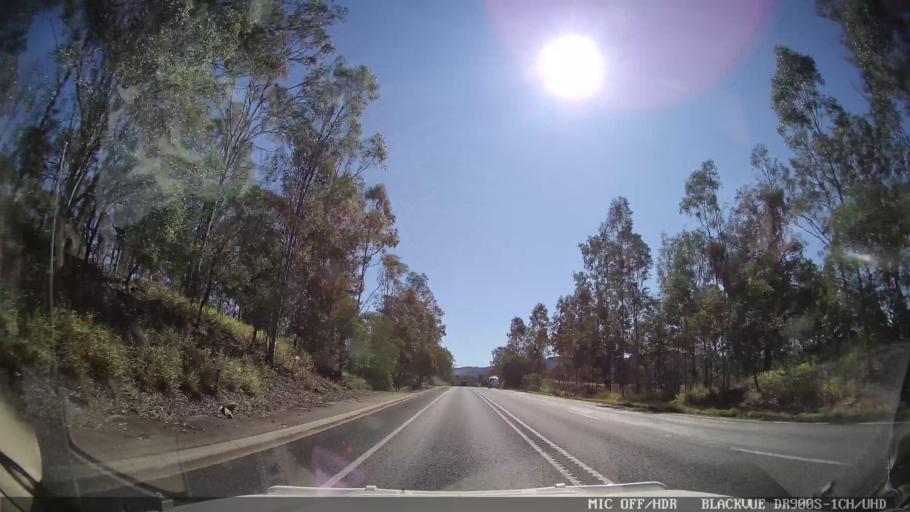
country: AU
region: Queensland
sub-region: Gympie Regional Council
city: Gympie
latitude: -26.0006
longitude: 152.5665
